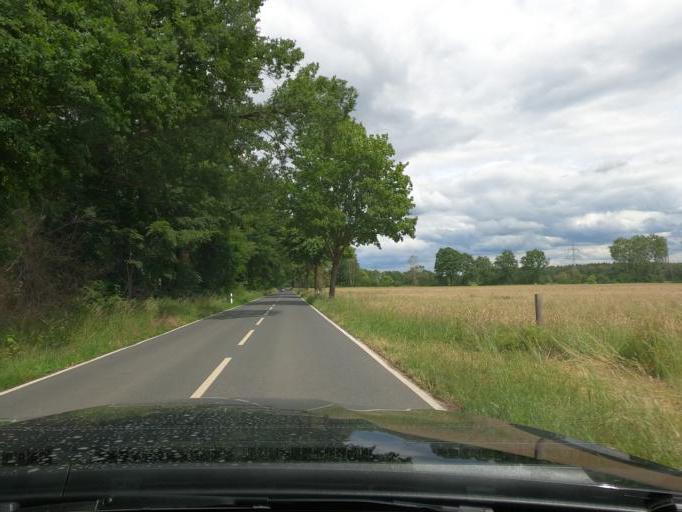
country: DE
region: Lower Saxony
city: Lehrte
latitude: 52.4038
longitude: 9.9293
